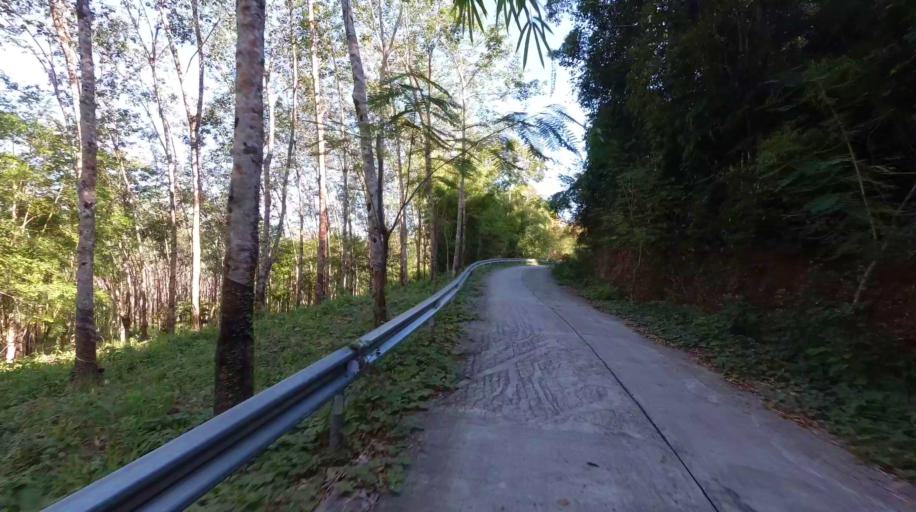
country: TH
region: Trat
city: Ko Kut
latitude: 11.6264
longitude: 102.5564
